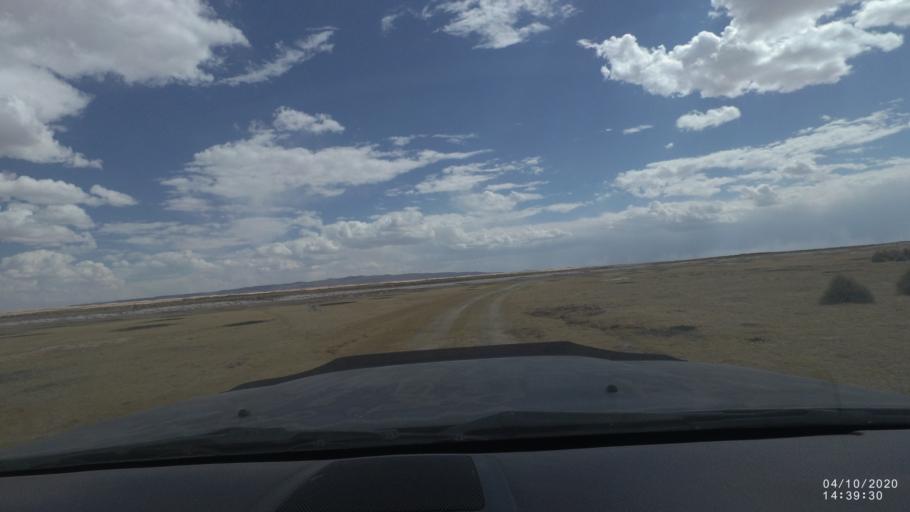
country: BO
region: Oruro
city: Poopo
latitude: -18.6778
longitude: -67.4863
